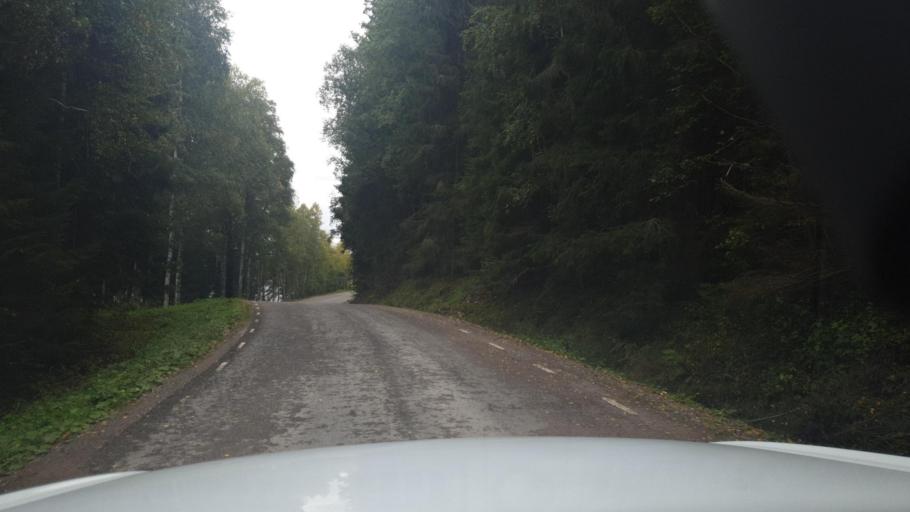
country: SE
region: Vaermland
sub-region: Eda Kommun
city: Charlottenberg
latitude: 60.0276
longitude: 12.6092
